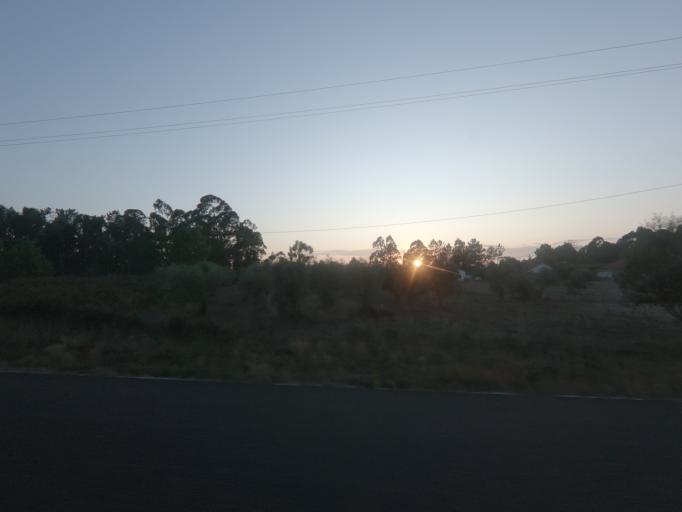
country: PT
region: Leiria
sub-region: Pombal
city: Pombal
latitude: 39.9004
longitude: -8.6902
